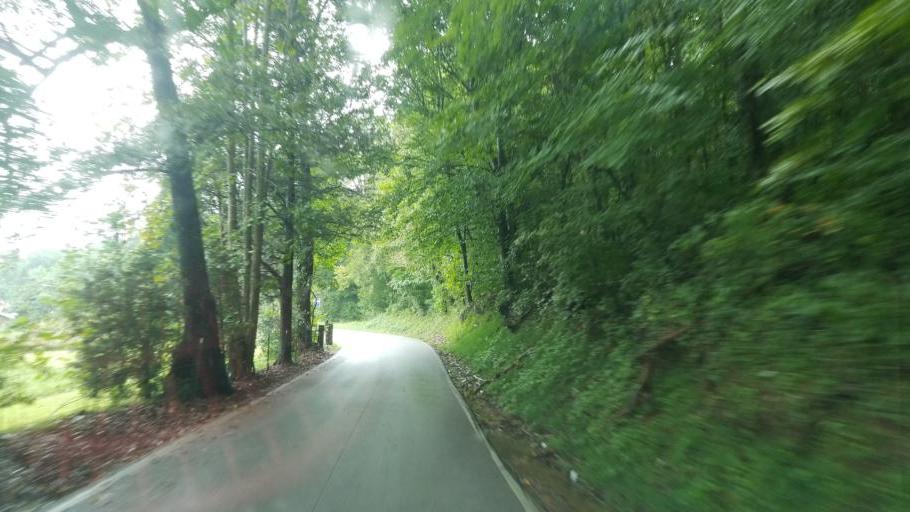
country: US
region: Kentucky
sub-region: Rowan County
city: Morehead
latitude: 38.1670
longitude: -83.4976
